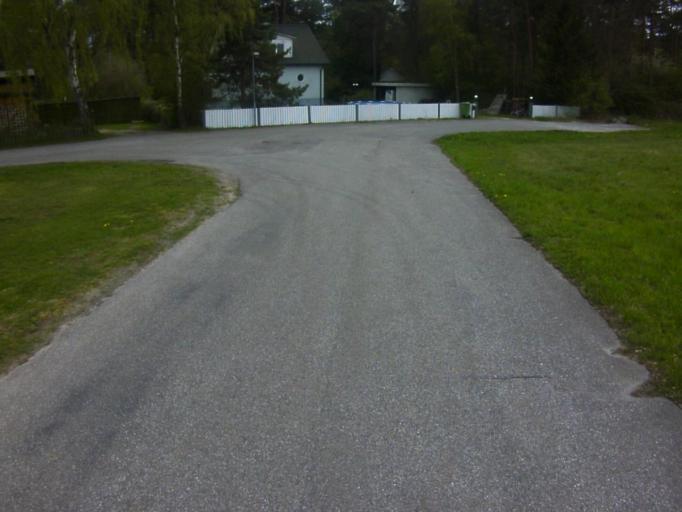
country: SE
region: Skane
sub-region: Kavlinge Kommun
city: Loddekopinge
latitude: 55.7576
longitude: 12.9981
